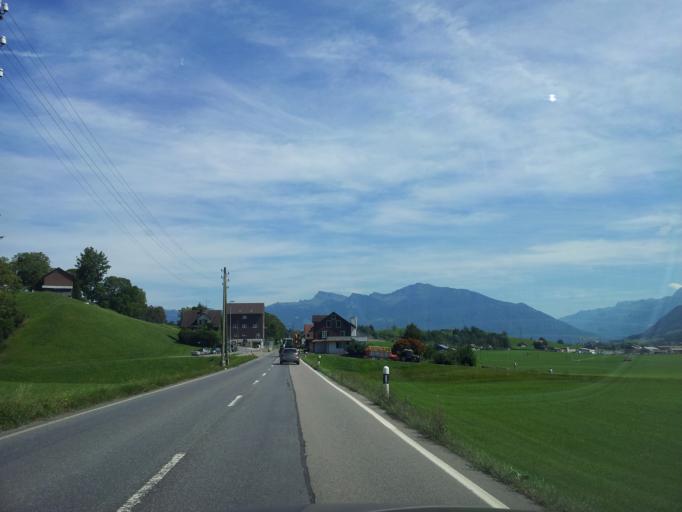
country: CH
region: Schwyz
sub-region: Bezirk March
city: Schubelbach
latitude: 47.1917
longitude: 8.9158
